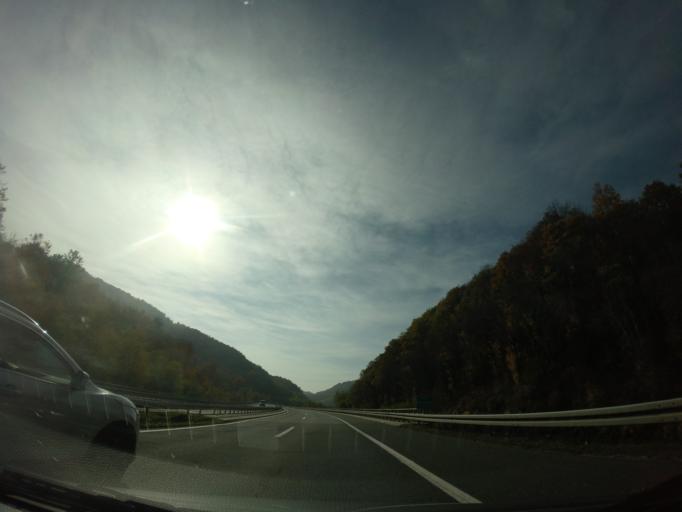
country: HR
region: Varazdinska
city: Remetinec
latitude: 46.1243
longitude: 16.3029
